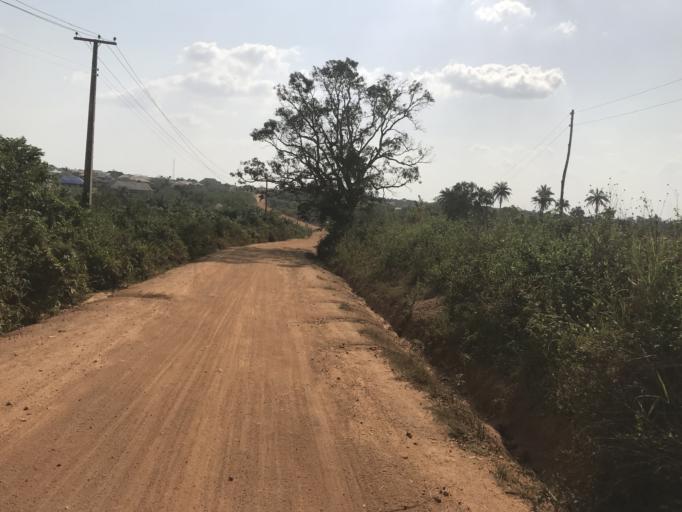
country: NG
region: Osun
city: Osogbo
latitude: 7.8215
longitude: 4.5652
